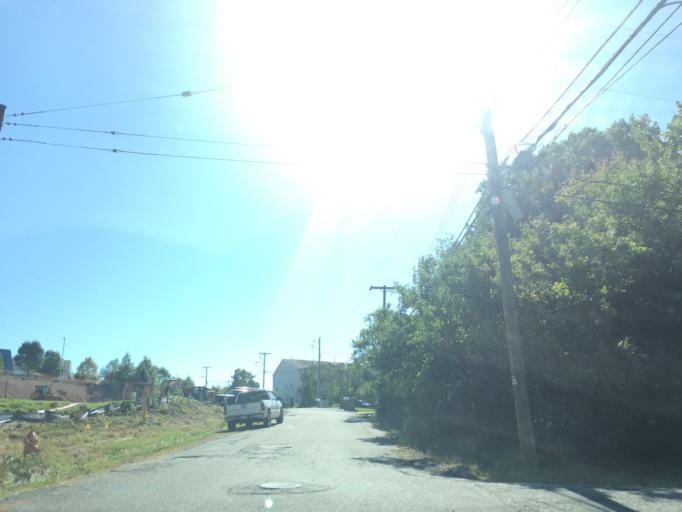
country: US
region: Maryland
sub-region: Baltimore County
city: Rossville
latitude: 39.3498
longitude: -76.4894
